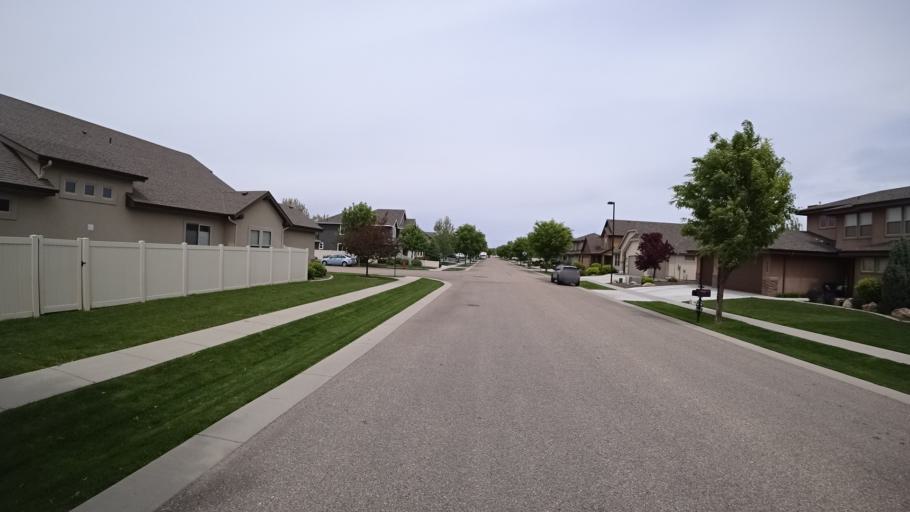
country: US
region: Idaho
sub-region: Ada County
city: Meridian
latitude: 43.5650
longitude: -116.3644
